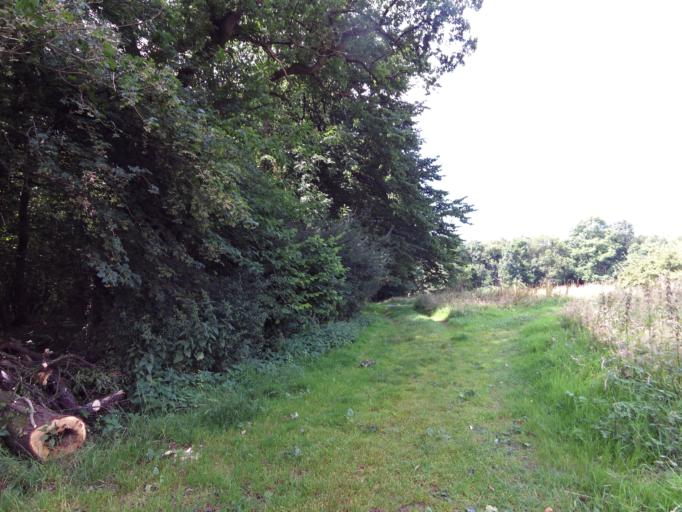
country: DE
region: North Rhine-Westphalia
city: Hemer
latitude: 51.3816
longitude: 7.7875
